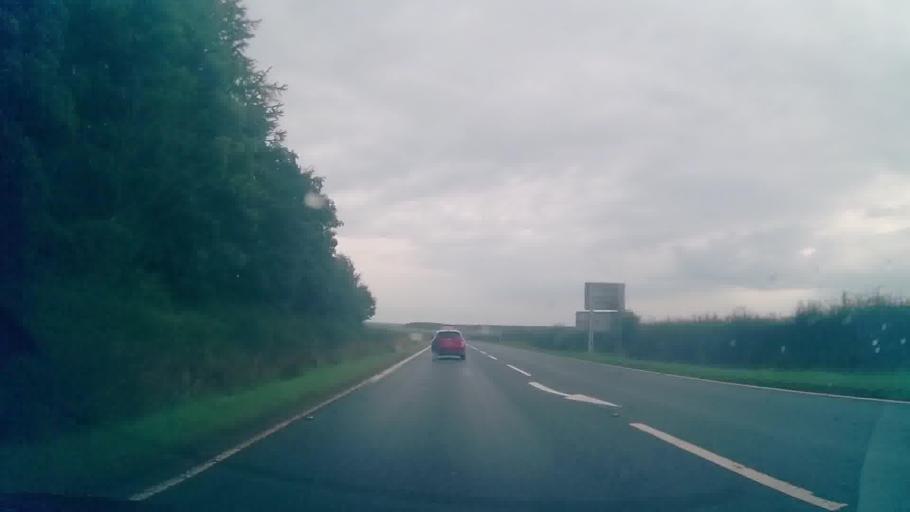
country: GB
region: Scotland
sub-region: Dumfries and Galloway
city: Annan
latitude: 55.0071
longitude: -3.3317
